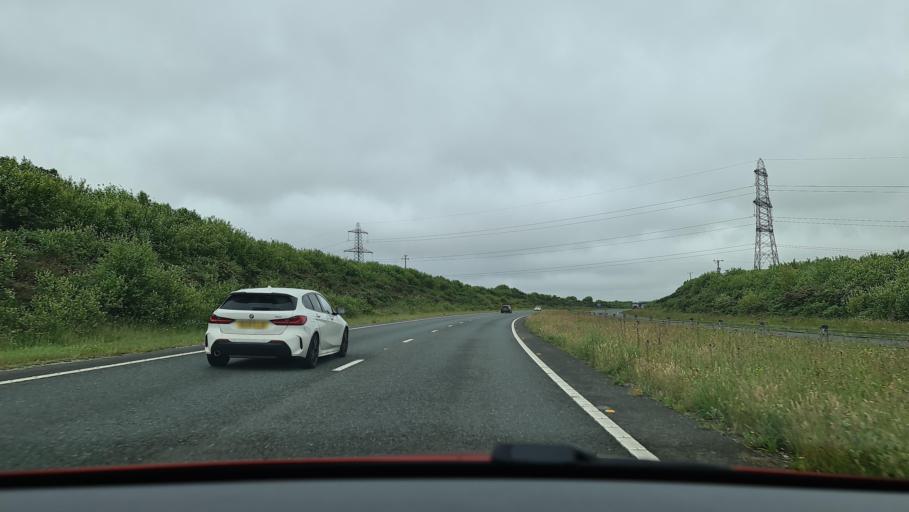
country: GB
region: England
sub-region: Cornwall
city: Roche
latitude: 50.4188
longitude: -4.8395
